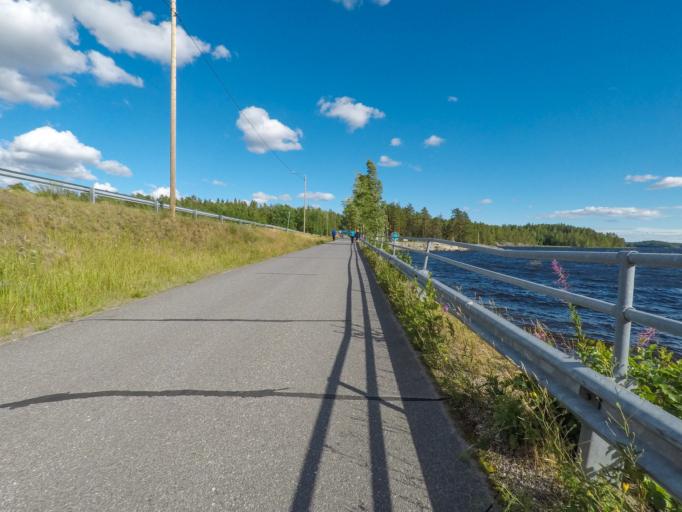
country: FI
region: South Karelia
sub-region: Lappeenranta
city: Lappeenranta
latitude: 61.1001
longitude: 28.1297
